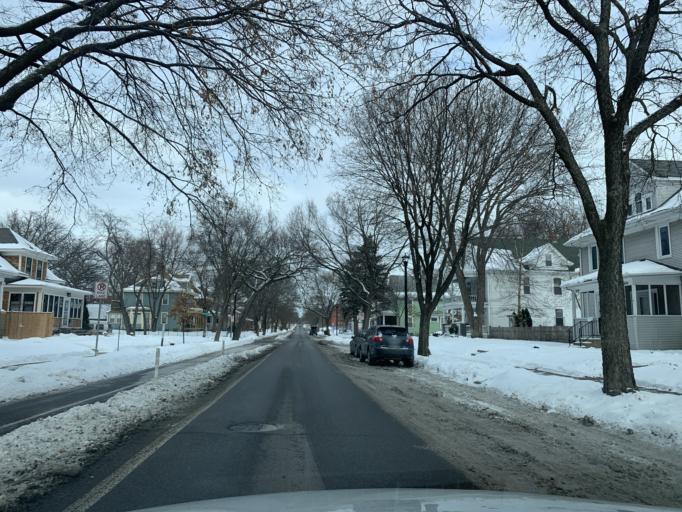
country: US
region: Minnesota
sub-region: Hennepin County
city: Minneapolis
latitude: 44.9956
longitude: -93.2941
